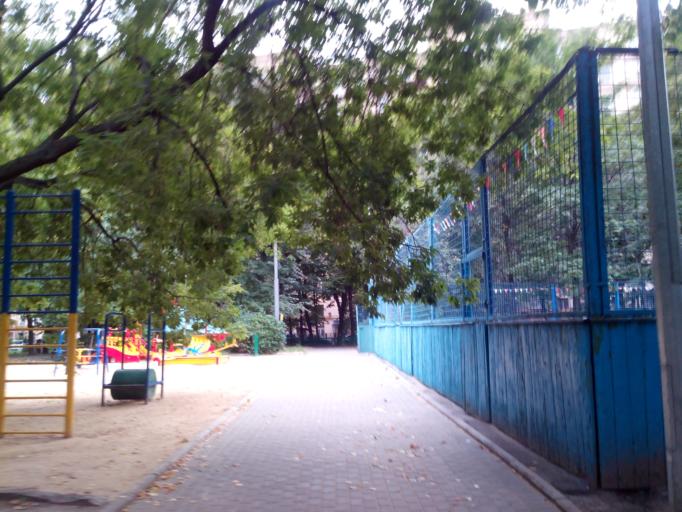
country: RU
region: Moskovskaya
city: Presnenskiy
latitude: 55.7422
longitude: 37.5375
